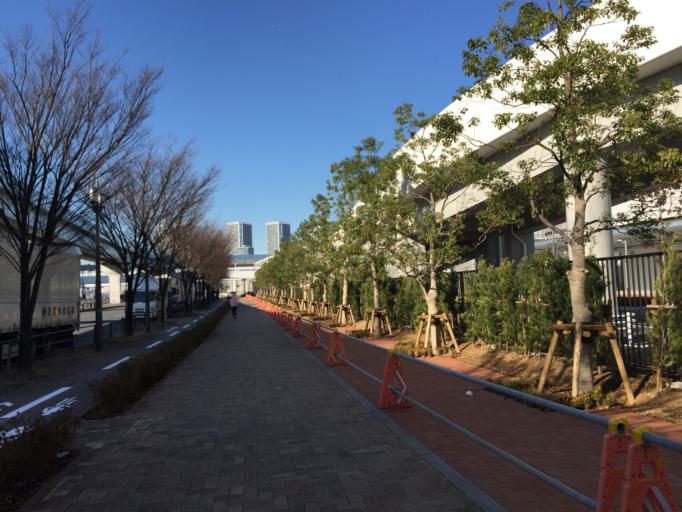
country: JP
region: Tokyo
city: Tokyo
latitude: 35.6437
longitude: 139.7862
